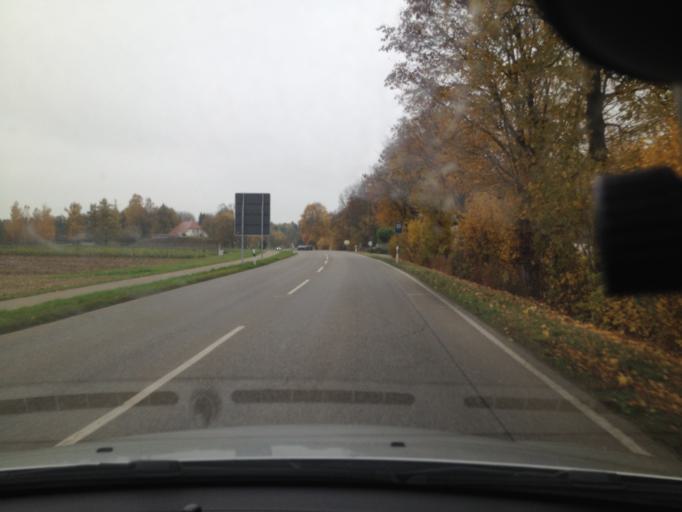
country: DE
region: Bavaria
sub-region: Swabia
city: Hiltenfingen
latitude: 48.1705
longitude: 10.7360
